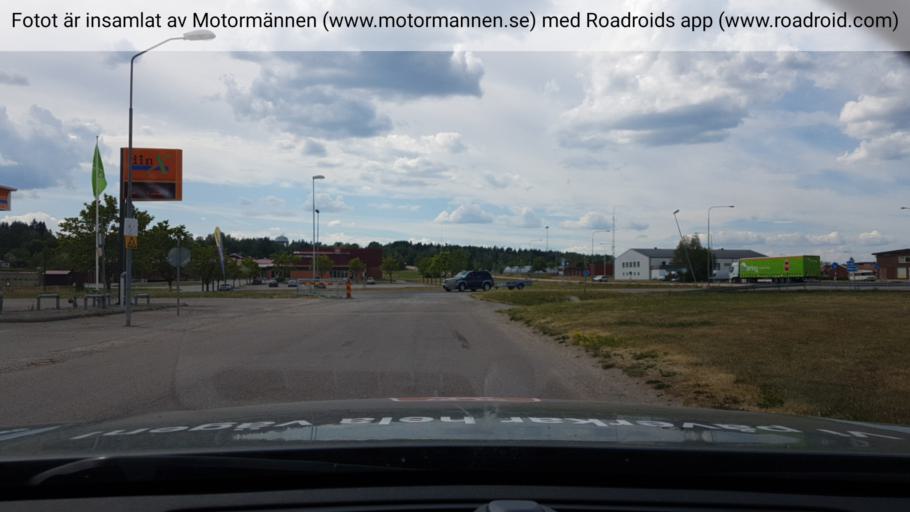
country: SE
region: Uppsala
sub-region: Heby Kommun
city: Heby
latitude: 59.9354
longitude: 16.8585
